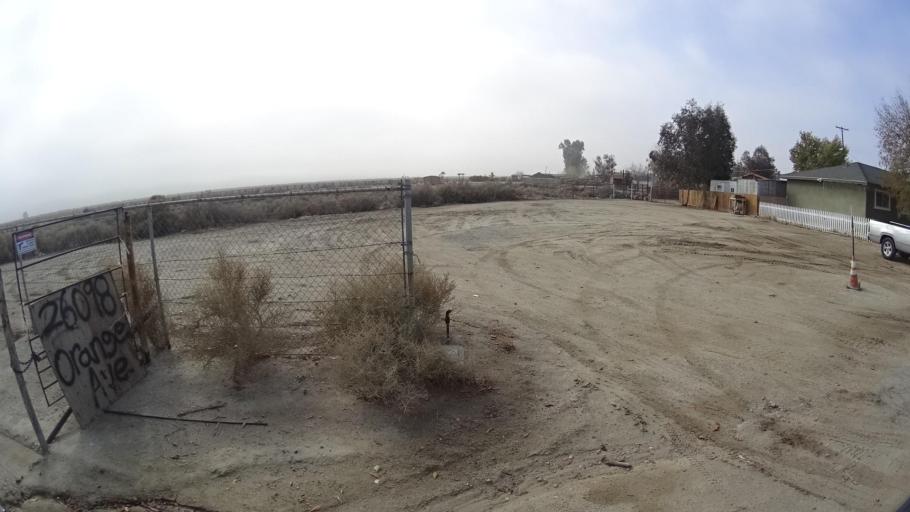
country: US
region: California
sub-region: Kern County
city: Ford City
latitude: 35.2039
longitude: -119.4047
